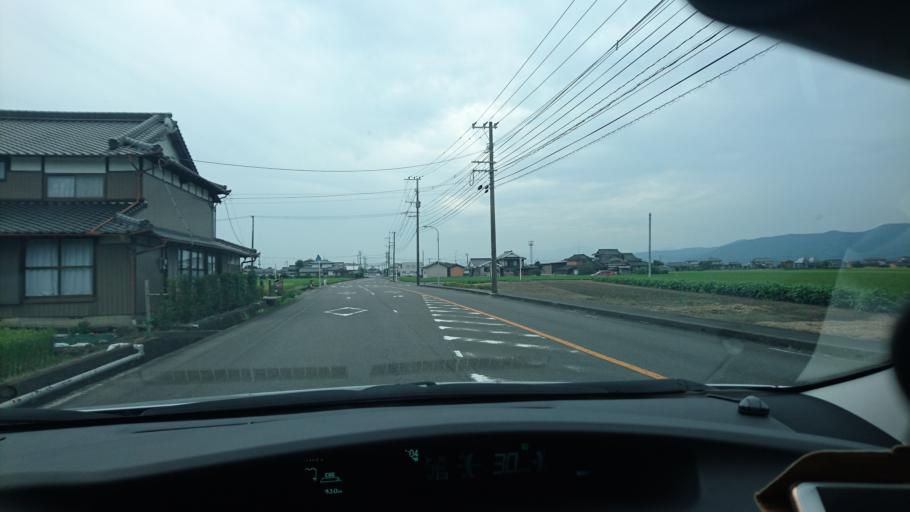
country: JP
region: Saga Prefecture
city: Takeocho-takeo
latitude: 33.2111
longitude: 130.1209
